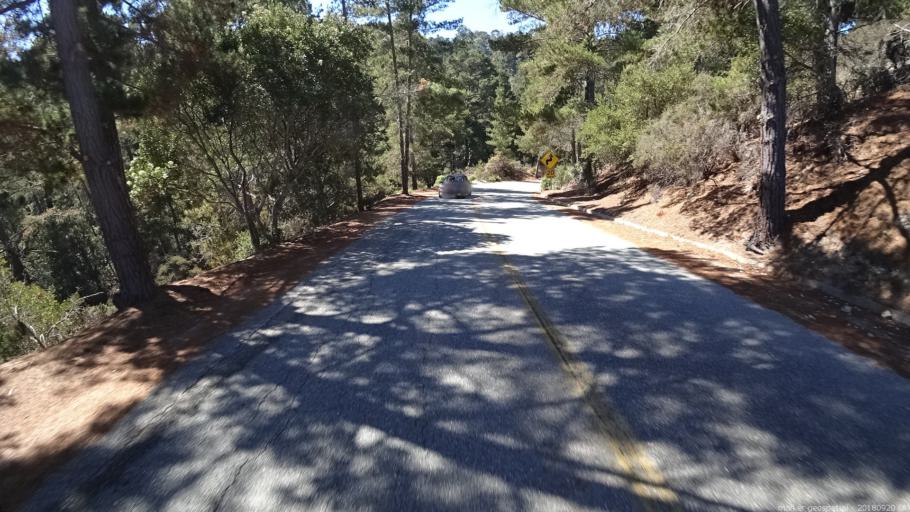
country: US
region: California
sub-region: Monterey County
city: Del Rey Oaks
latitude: 36.5679
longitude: -121.8587
